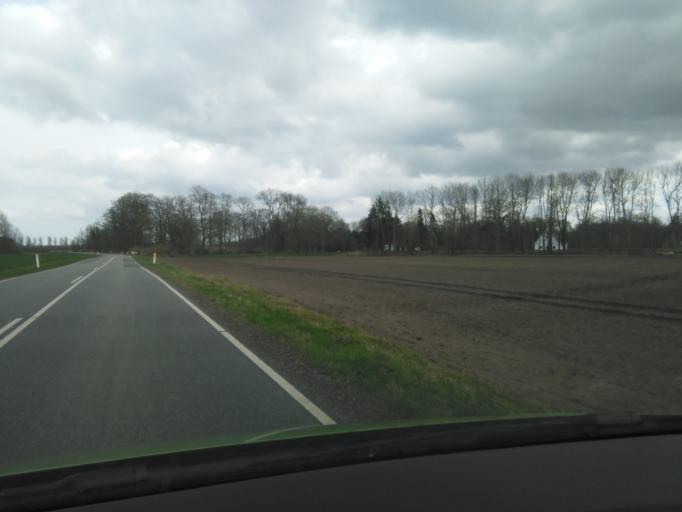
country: DK
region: South Denmark
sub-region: Nordfyns Kommune
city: Bogense
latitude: 55.5670
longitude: 10.1437
